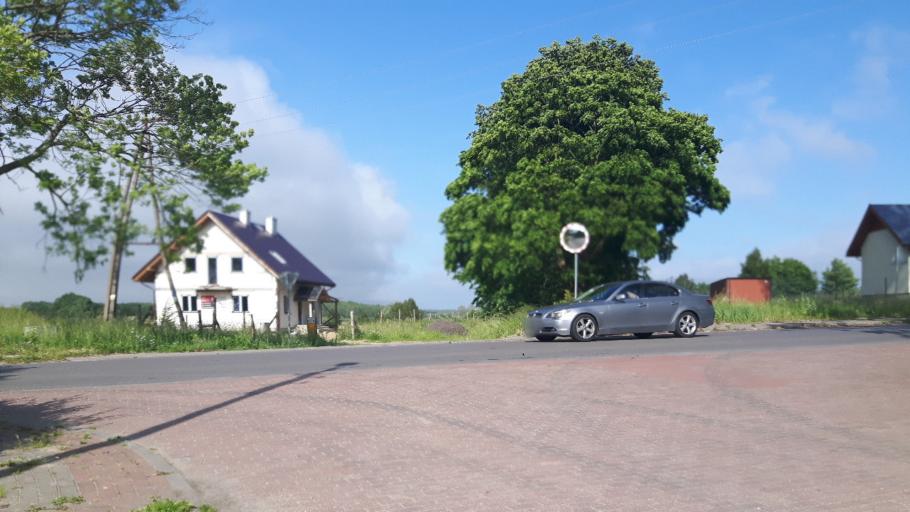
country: PL
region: Pomeranian Voivodeship
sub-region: Slupsk
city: Slupsk
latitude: 54.6140
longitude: 17.0340
